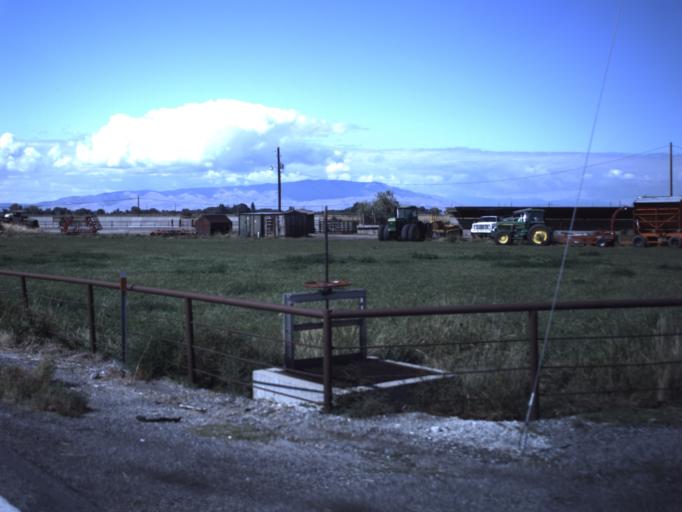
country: US
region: Utah
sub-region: Utah County
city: Spanish Fork
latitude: 40.1155
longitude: -111.6832
